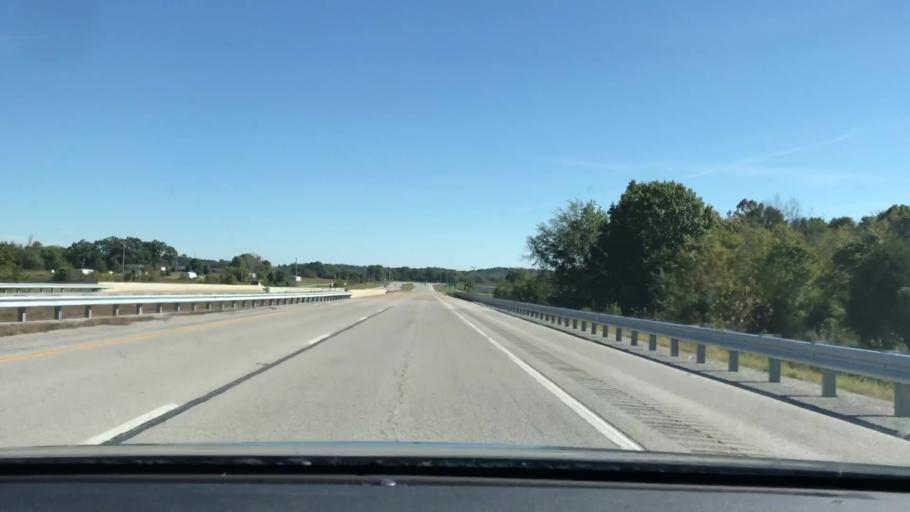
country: US
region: Kentucky
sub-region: Todd County
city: Elkton
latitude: 36.8213
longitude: -87.1686
